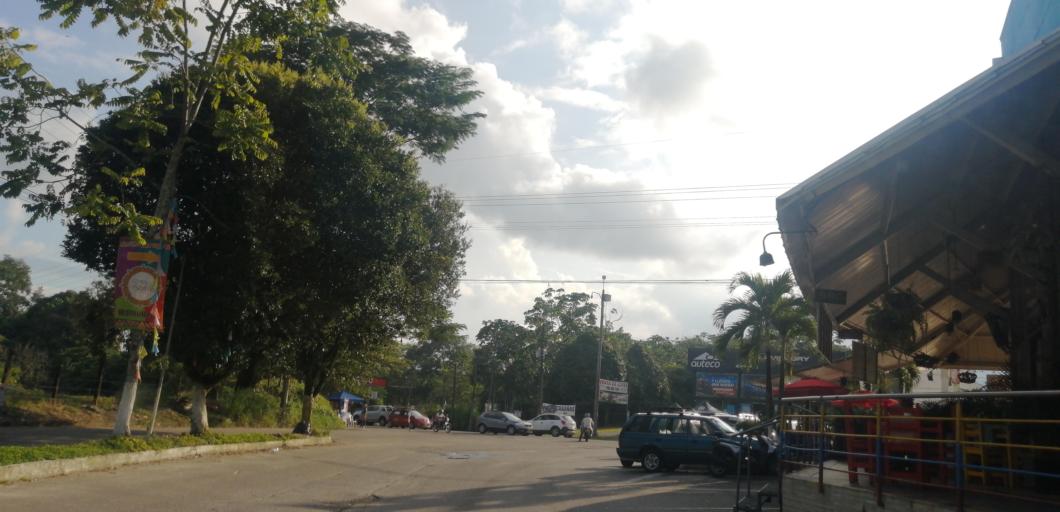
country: CO
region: Meta
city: Acacias
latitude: 3.9782
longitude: -73.7665
